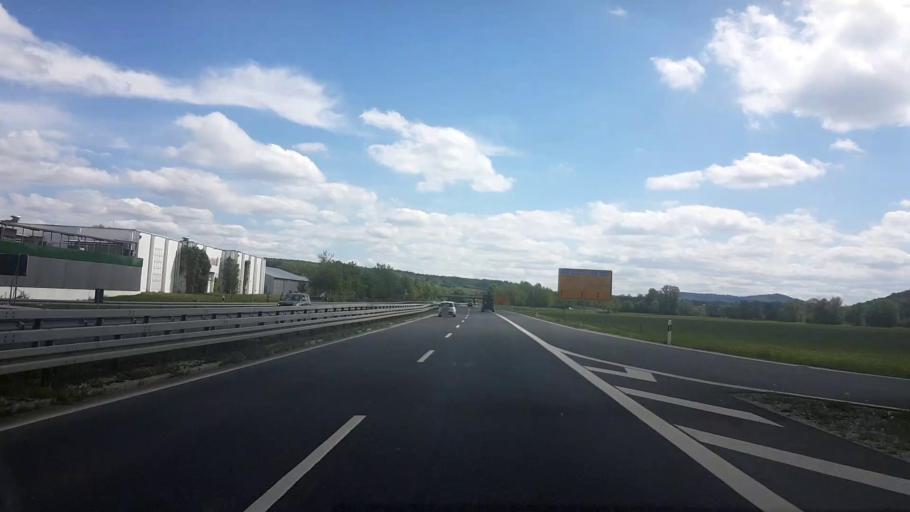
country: DE
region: Bavaria
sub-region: Upper Franconia
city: Niederfullbach
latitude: 50.2281
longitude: 10.9780
